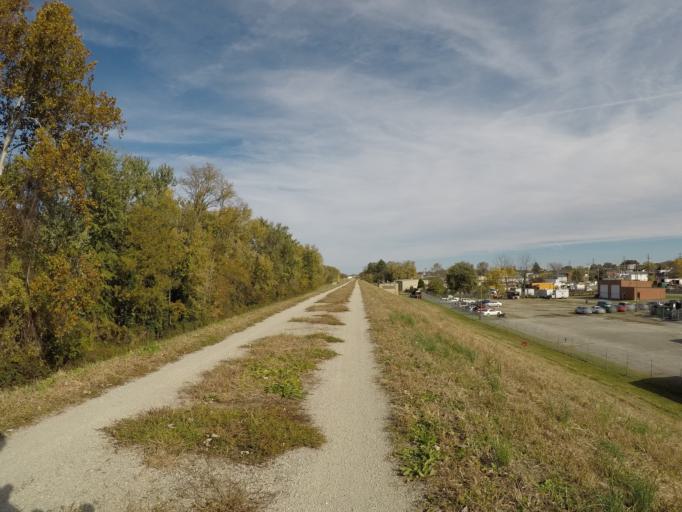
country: US
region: West Virginia
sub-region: Cabell County
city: Huntington
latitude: 38.4177
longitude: -82.4699
